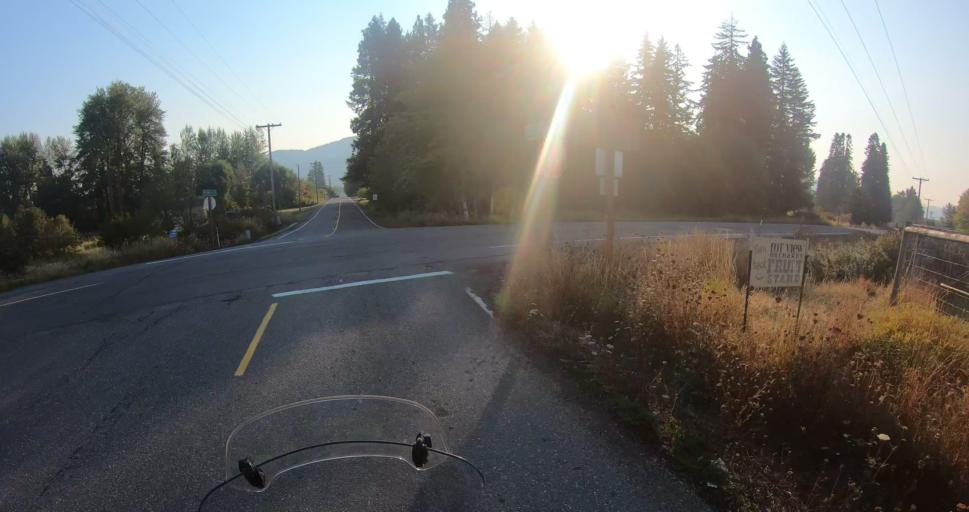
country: US
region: Oregon
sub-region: Hood River County
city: Odell
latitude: 45.5418
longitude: -121.6060
